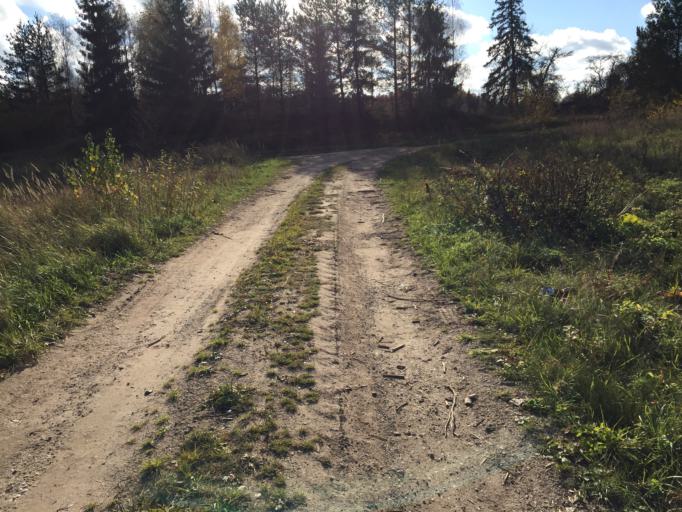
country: LV
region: Tukuma Rajons
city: Tukums
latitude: 56.9623
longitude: 22.9912
